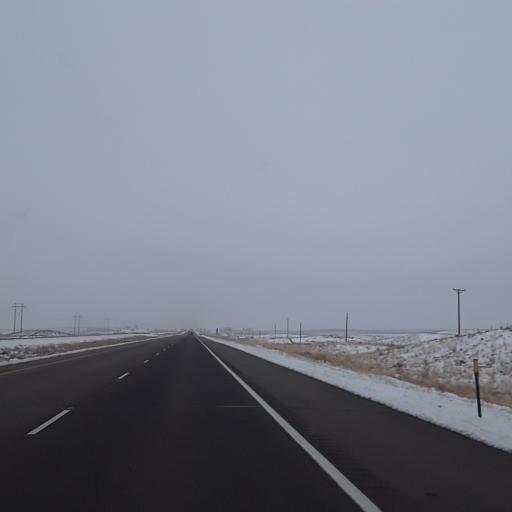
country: US
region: Colorado
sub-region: Logan County
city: Sterling
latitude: 40.4847
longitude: -103.2751
